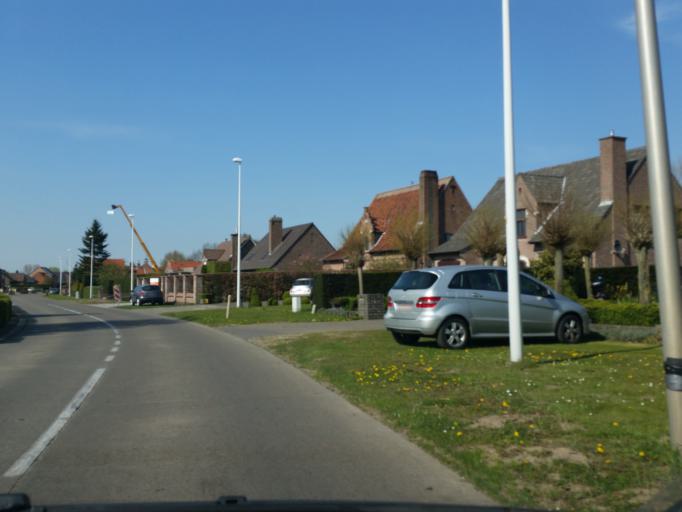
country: BE
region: Flanders
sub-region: Provincie Oost-Vlaanderen
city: Sint-Gillis-Waas
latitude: 51.2005
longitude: 4.1481
